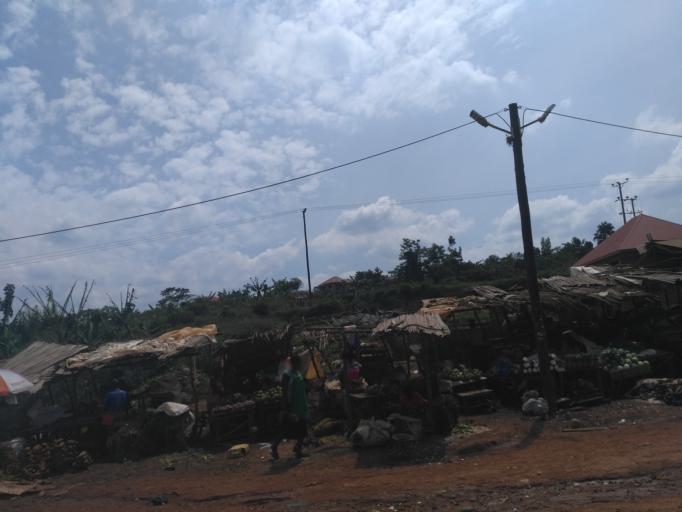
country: UG
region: Central Region
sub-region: Wakiso District
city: Bweyogerere
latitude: 0.4838
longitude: 32.6091
